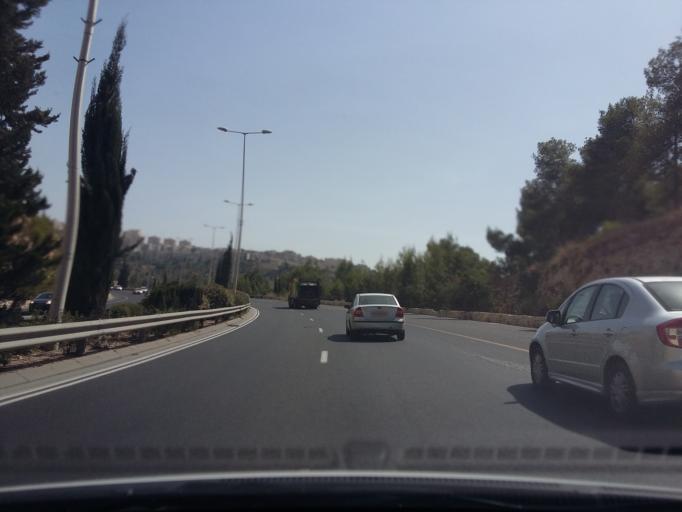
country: IL
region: Jerusalem
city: West Jerusalem
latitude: 31.8052
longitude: 35.2055
